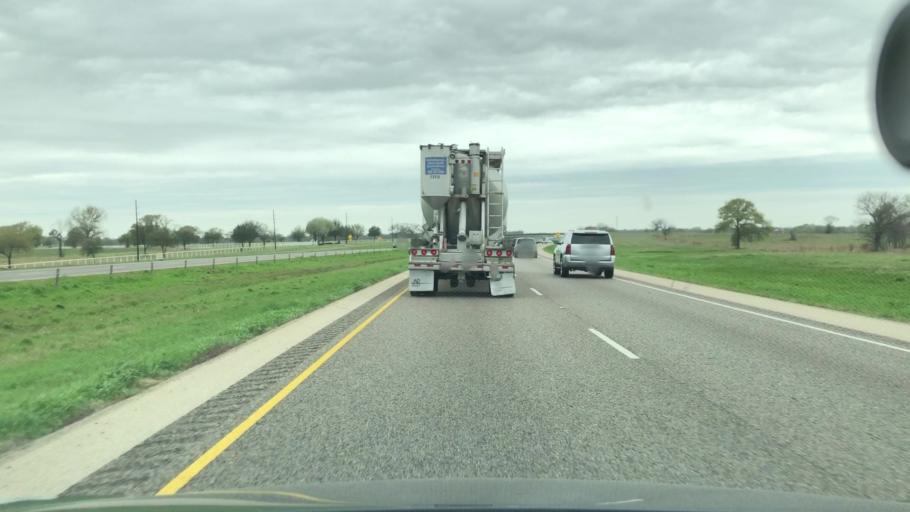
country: US
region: Texas
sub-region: Madison County
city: Madisonville
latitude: 31.0430
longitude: -95.9440
